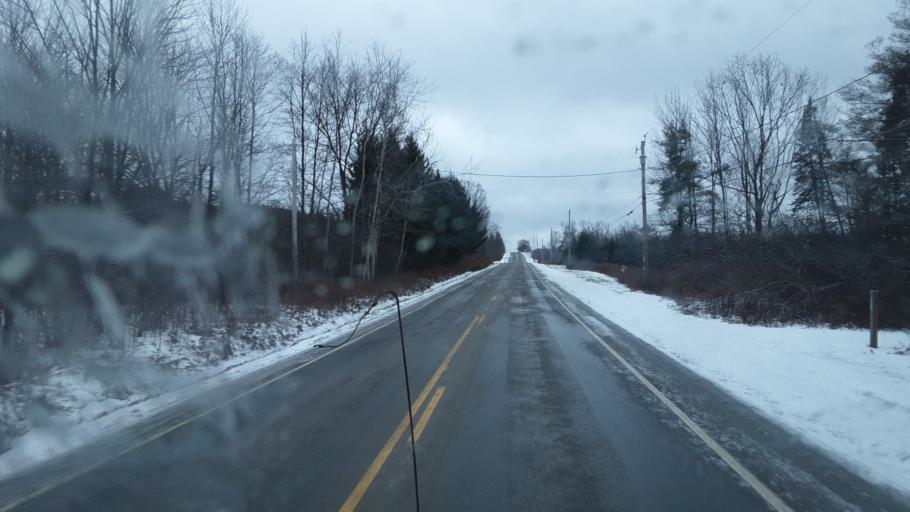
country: US
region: New York
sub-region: Allegany County
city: Friendship
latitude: 42.2552
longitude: -78.1476
